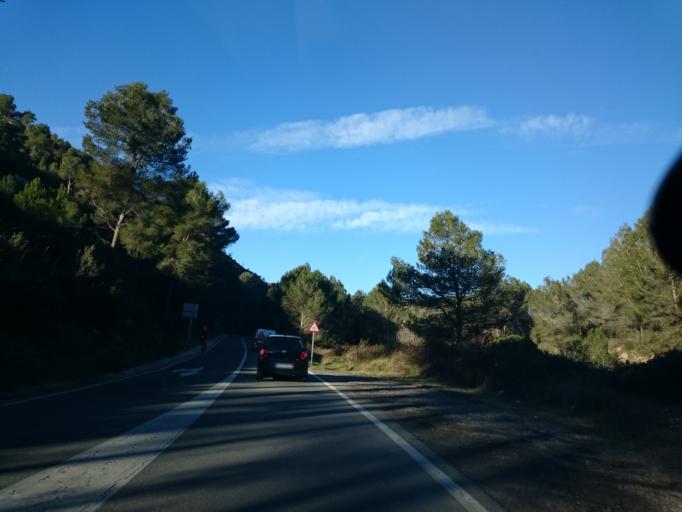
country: ES
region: Catalonia
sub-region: Provincia de Barcelona
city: Sant Pere de Ribes
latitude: 41.2872
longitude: 1.7410
